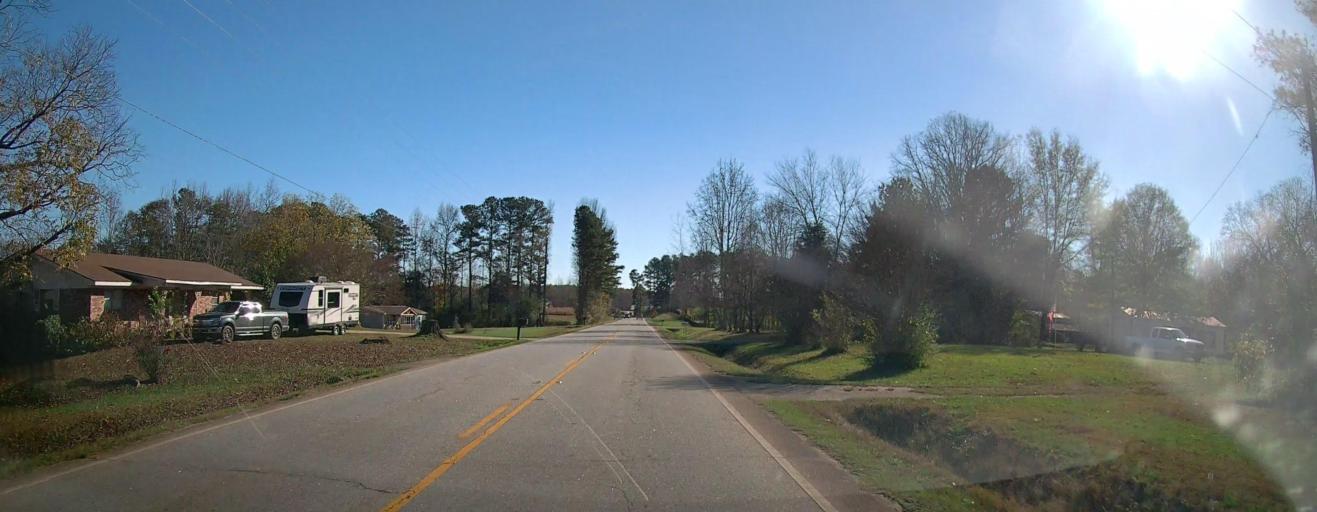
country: US
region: Georgia
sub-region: Hall County
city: Lula
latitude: 34.4482
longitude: -83.7277
